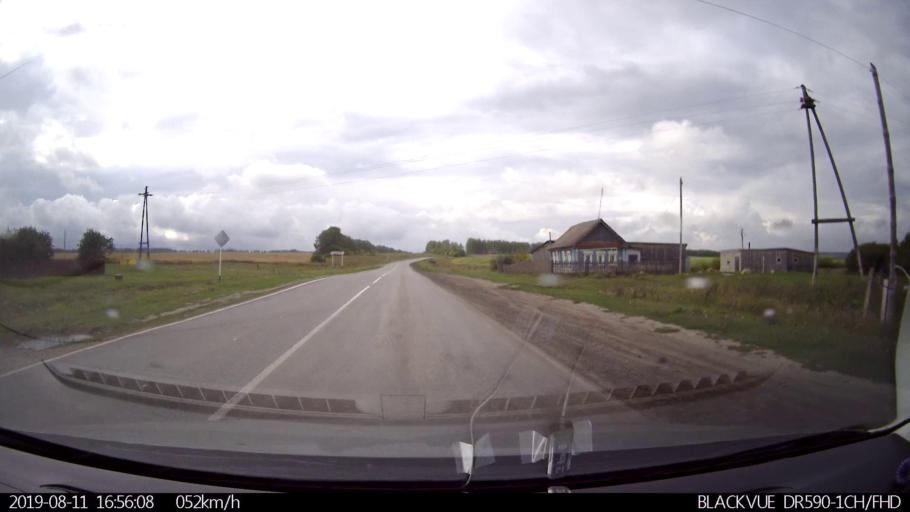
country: RU
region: Ulyanovsk
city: Mayna
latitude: 54.2858
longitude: 47.6567
